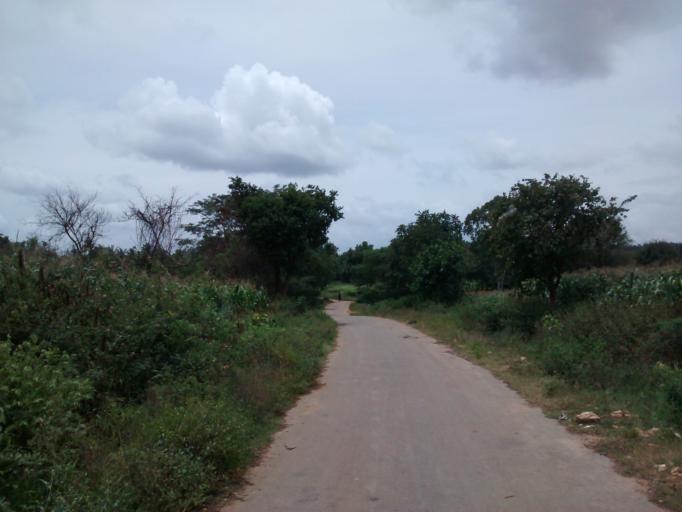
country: IN
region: Karnataka
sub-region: Hassan
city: Hassan
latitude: 12.9160
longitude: 76.1309
